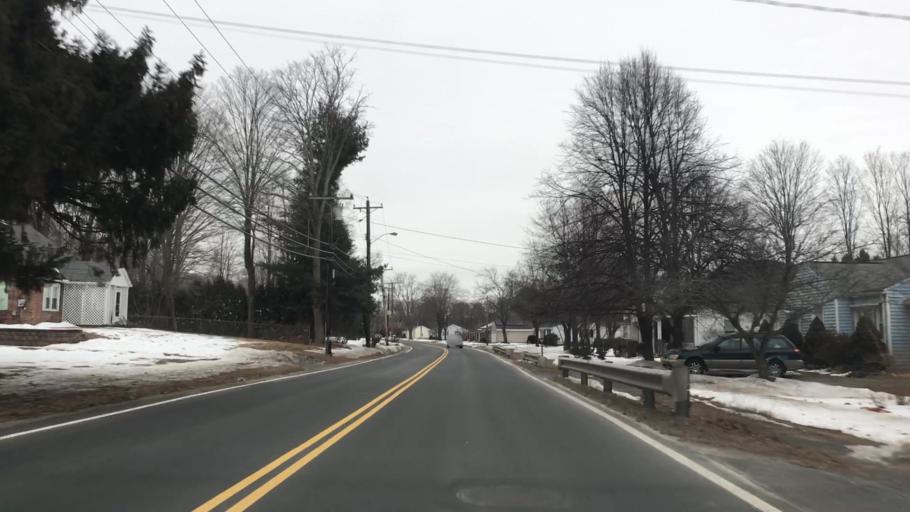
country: US
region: Massachusetts
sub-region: Hampden County
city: West Springfield
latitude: 42.0813
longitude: -72.6791
